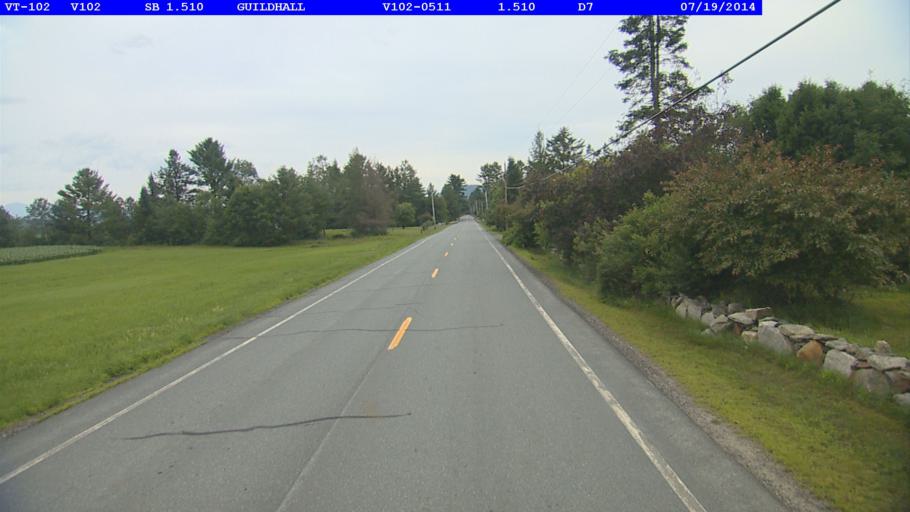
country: US
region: New Hampshire
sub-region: Coos County
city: Lancaster
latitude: 44.5172
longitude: -71.5946
